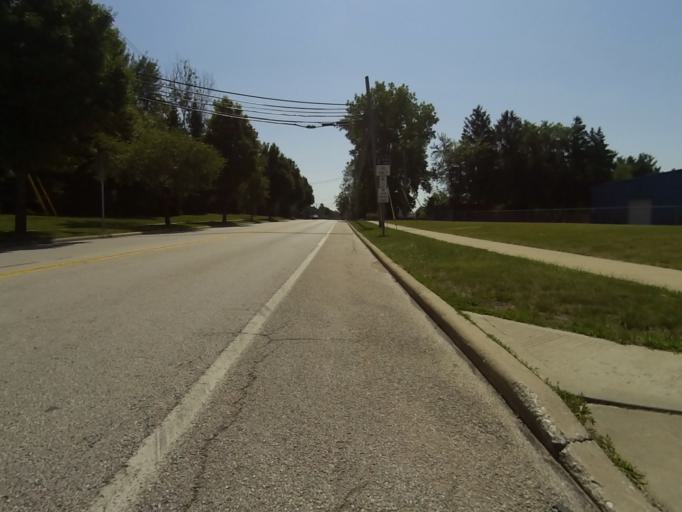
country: US
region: Ohio
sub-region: Portage County
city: Kent
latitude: 41.1655
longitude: -81.3886
